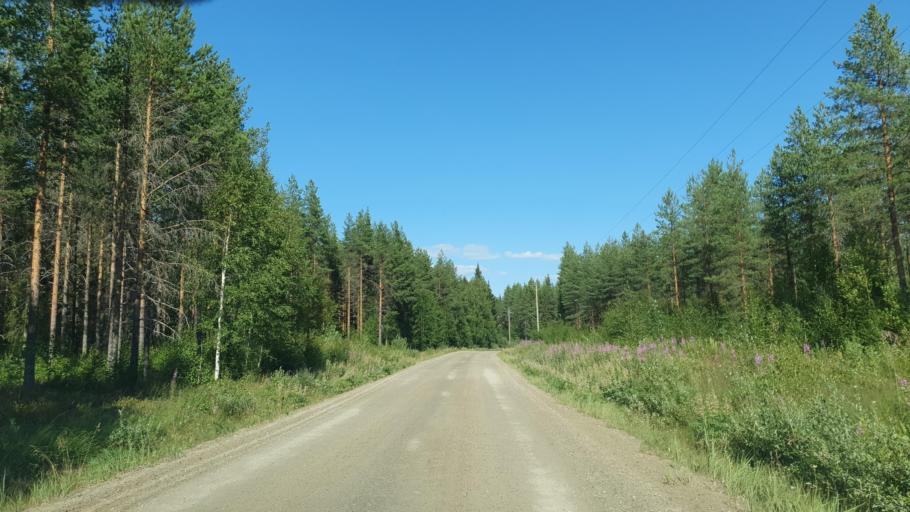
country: FI
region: Kainuu
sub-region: Kehys-Kainuu
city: Kuhmo
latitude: 64.0516
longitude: 29.5654
